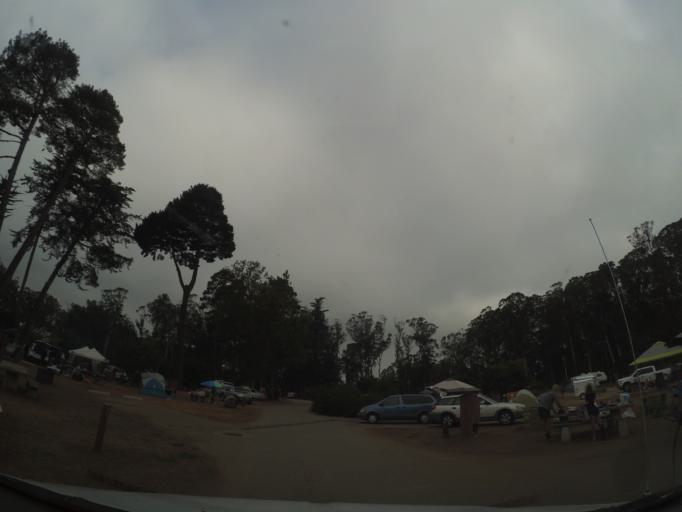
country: US
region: California
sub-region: San Luis Obispo County
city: Morro Bay
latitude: 35.3468
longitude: -120.8388
